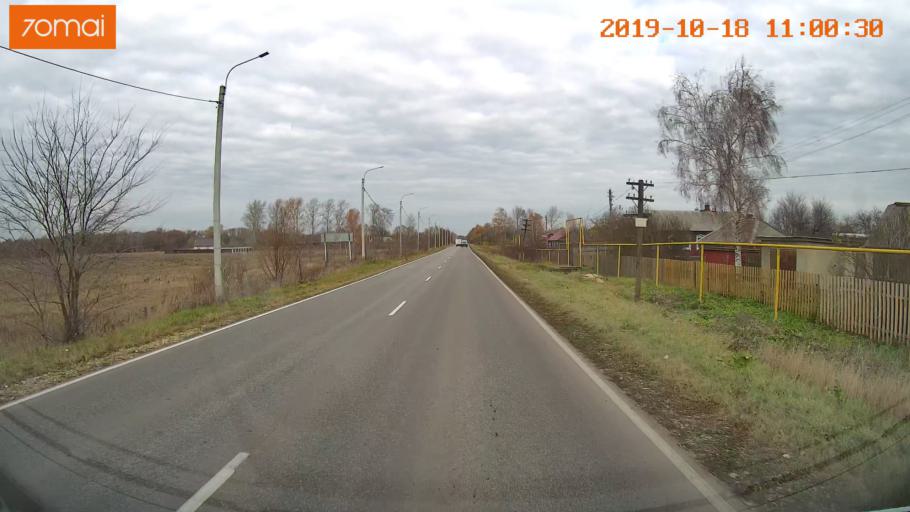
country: RU
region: Tula
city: Yepifan'
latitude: 53.8440
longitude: 38.5527
